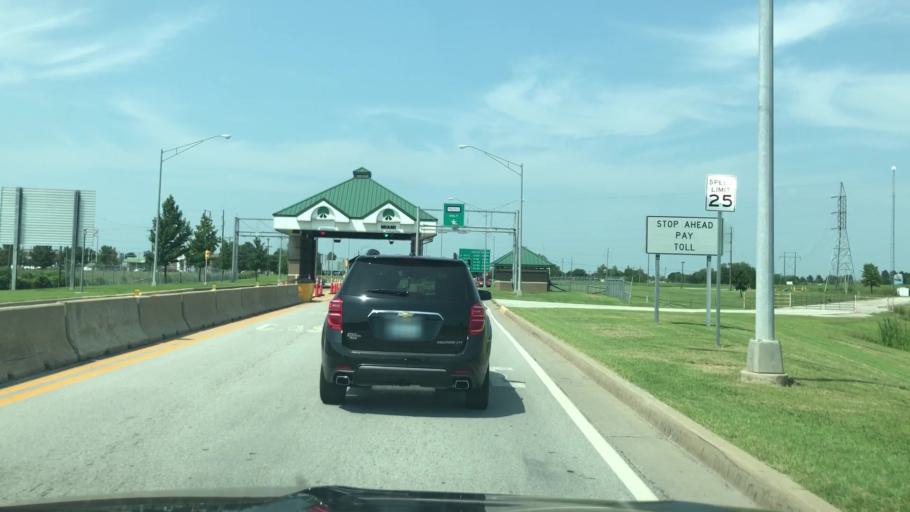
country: US
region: Oklahoma
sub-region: Ottawa County
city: Miami
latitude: 36.8679
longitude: -94.8518
